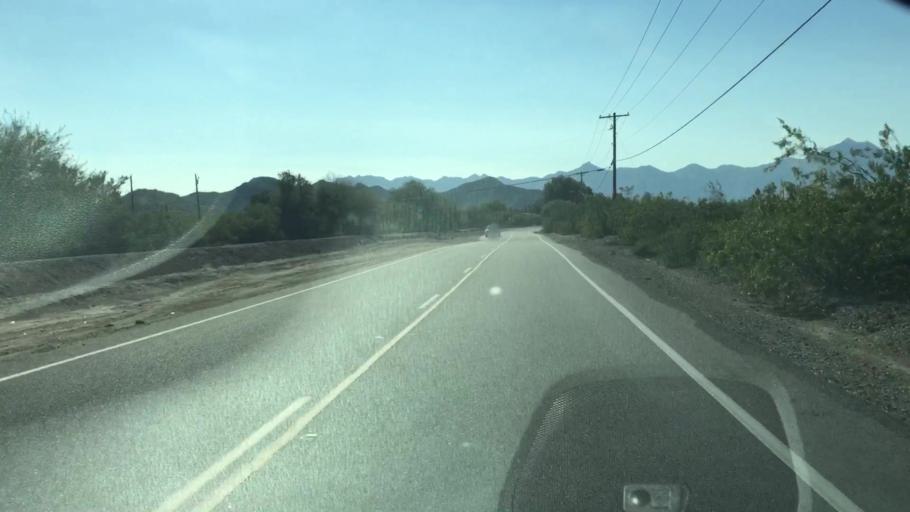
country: US
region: Arizona
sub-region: Maricopa County
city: Laveen
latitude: 33.3456
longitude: -112.1391
